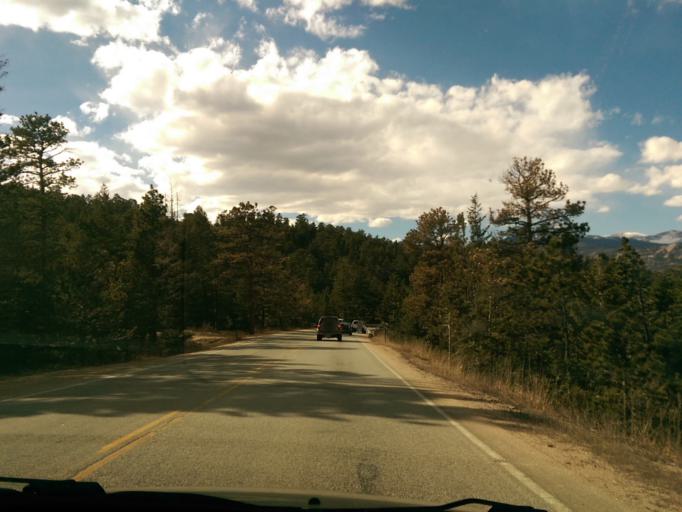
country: US
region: Colorado
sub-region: Larimer County
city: Estes Park
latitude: 40.3636
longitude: -105.4707
